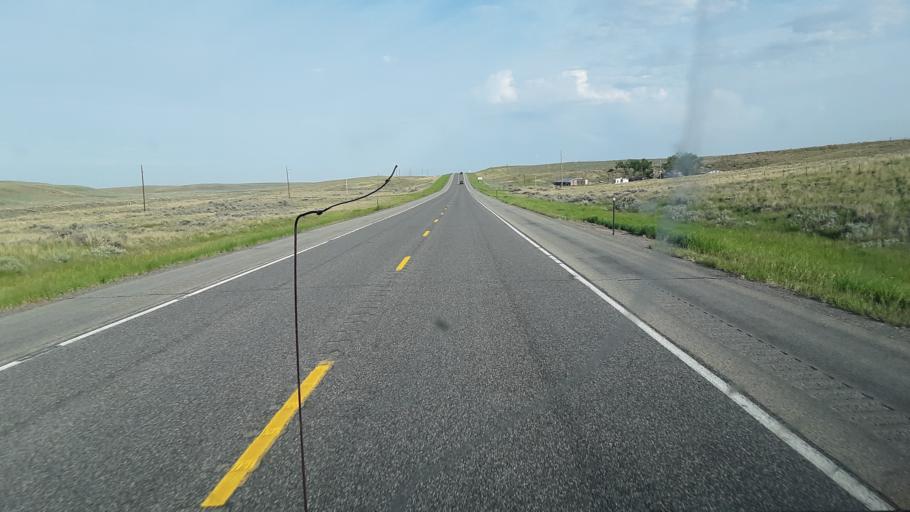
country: US
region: Wyoming
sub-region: Hot Springs County
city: Thermopolis
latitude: 43.1218
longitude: -107.3635
